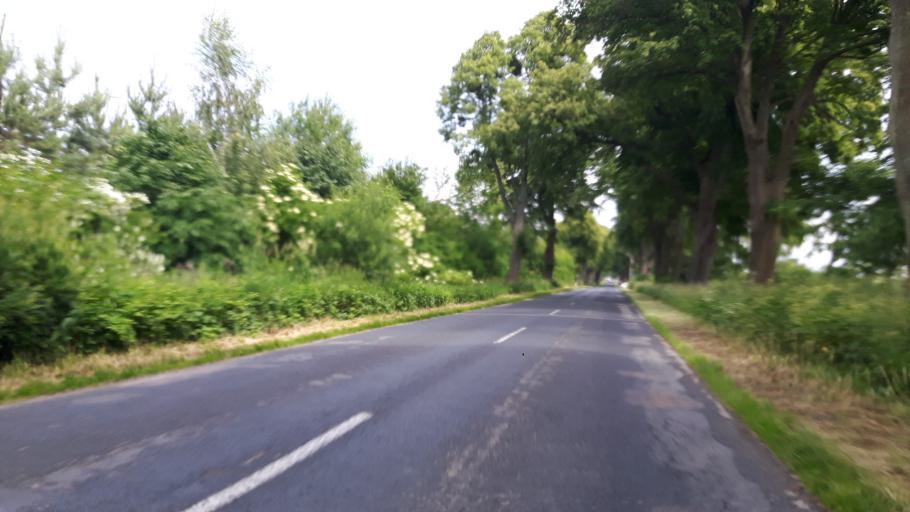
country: PL
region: Warmian-Masurian Voivodeship
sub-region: Powiat braniewski
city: Braniewo
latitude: 54.3638
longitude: 19.7595
